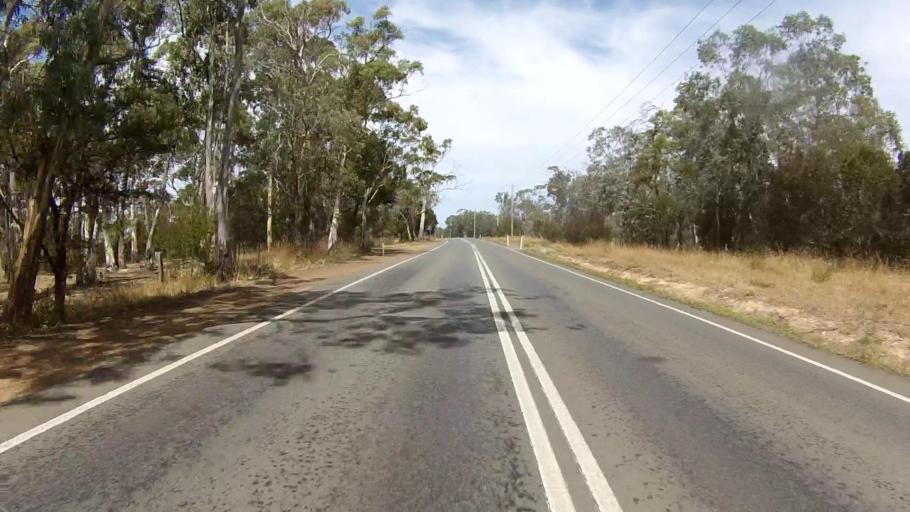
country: AU
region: Tasmania
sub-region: Clarence
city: Sandford
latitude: -42.9704
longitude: 147.5034
